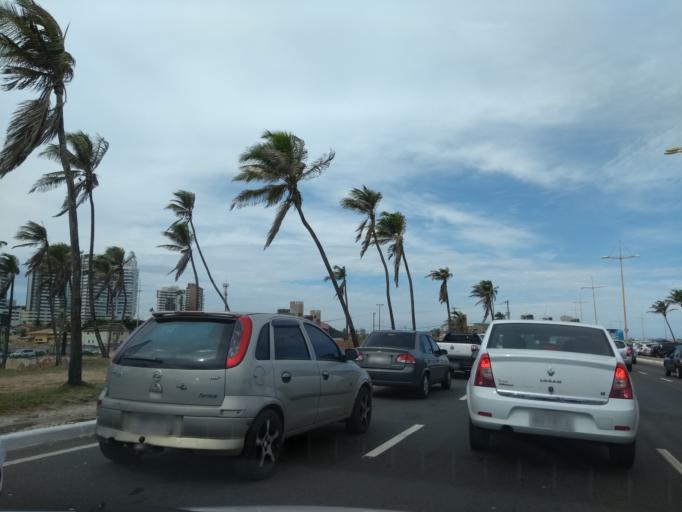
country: BR
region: Bahia
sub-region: Lauro De Freitas
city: Lauro de Freitas
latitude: -12.9662
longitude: -38.4044
